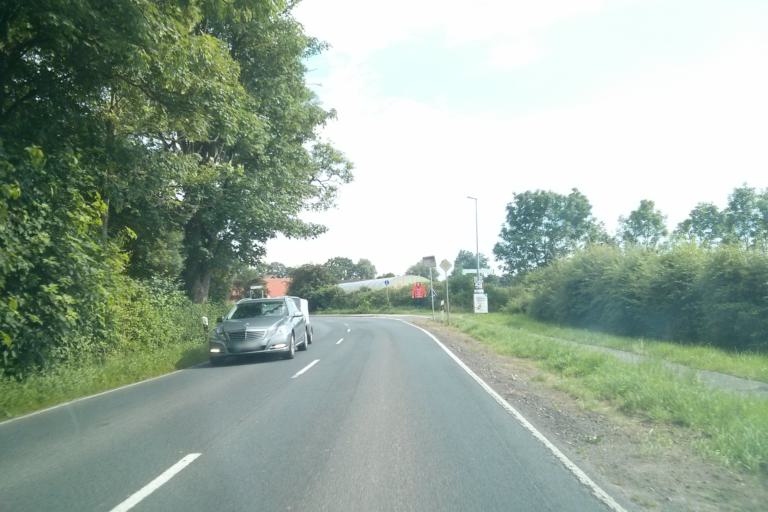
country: DE
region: Lower Saxony
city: Thedinghausen
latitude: 52.9764
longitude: 9.0463
